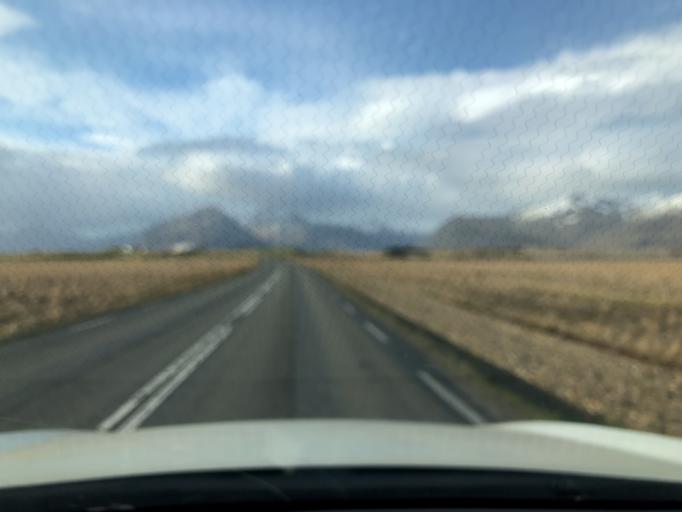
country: IS
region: East
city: Hoefn
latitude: 64.2709
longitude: -15.2024
